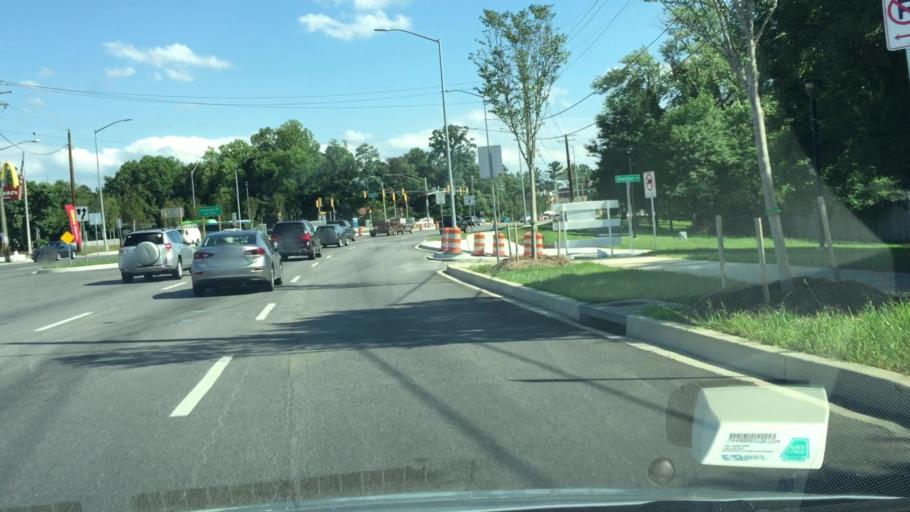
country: US
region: Maryland
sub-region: Montgomery County
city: Glenmont
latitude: 39.0596
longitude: -77.0507
